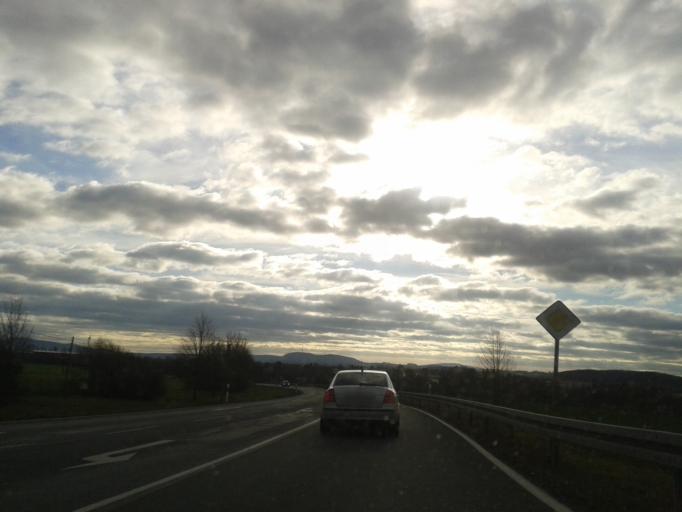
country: DE
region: Saxony
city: Weissenberg
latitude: 51.2049
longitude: 14.6640
